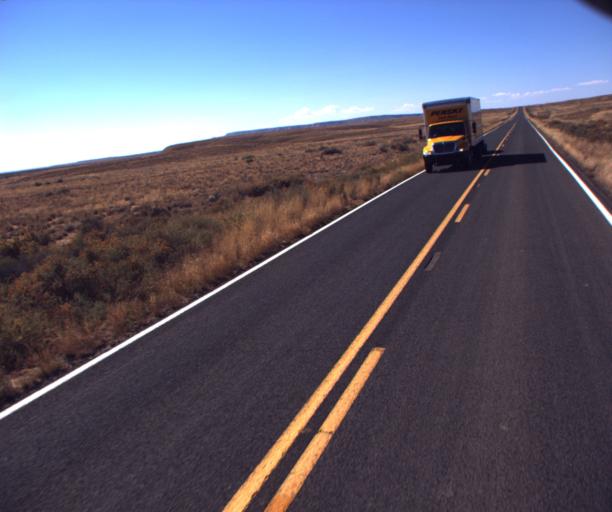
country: US
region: Arizona
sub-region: Navajo County
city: First Mesa
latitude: 35.9785
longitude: -110.7444
